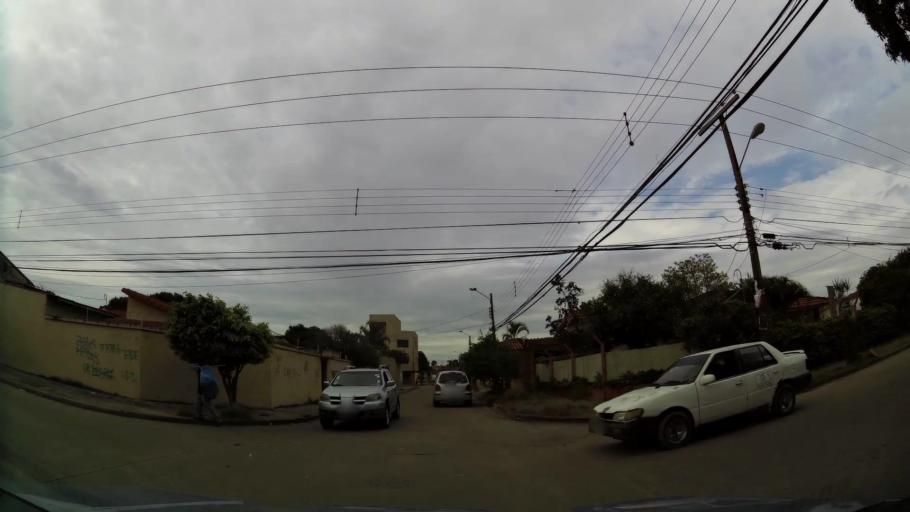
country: BO
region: Santa Cruz
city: Santa Cruz de la Sierra
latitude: -17.7661
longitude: -63.1641
